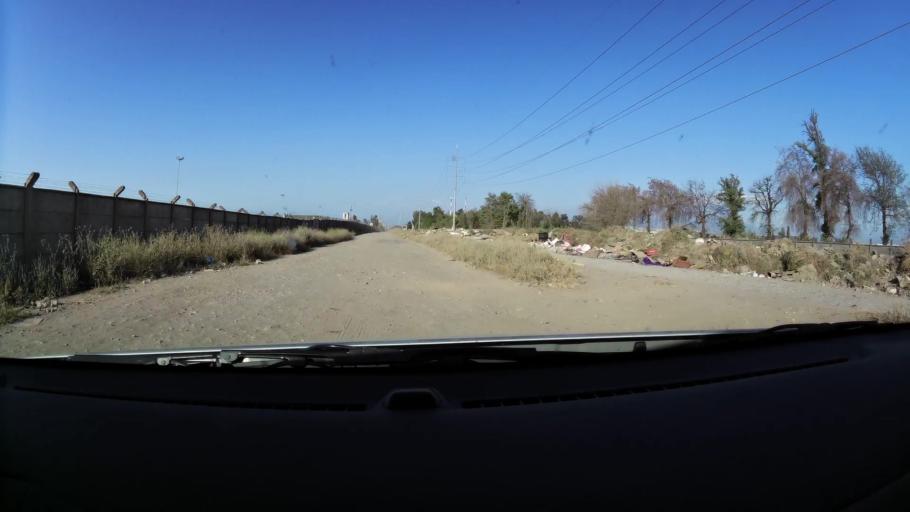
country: CL
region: Santiago Metropolitan
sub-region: Provincia de Maipo
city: San Bernardo
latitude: -33.5360
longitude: -70.7587
